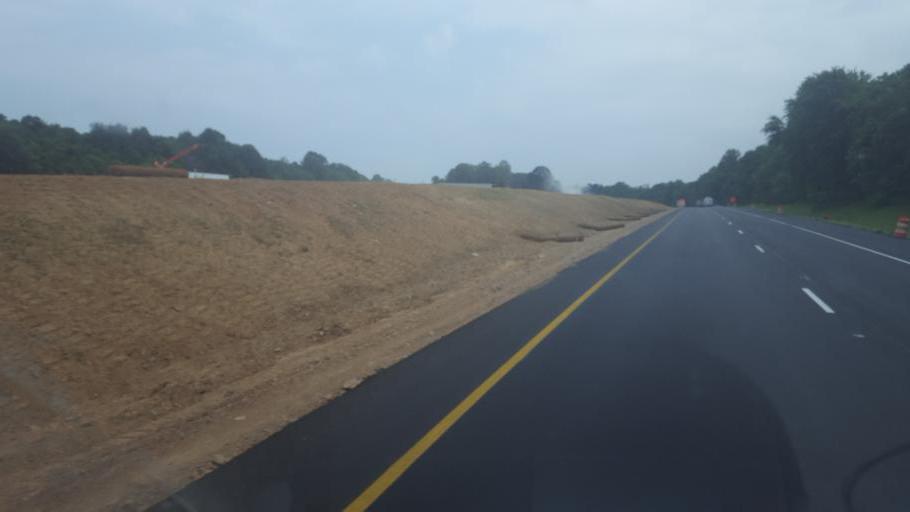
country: US
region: North Carolina
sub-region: Iredell County
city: Statesville
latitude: 35.8981
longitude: -80.8582
